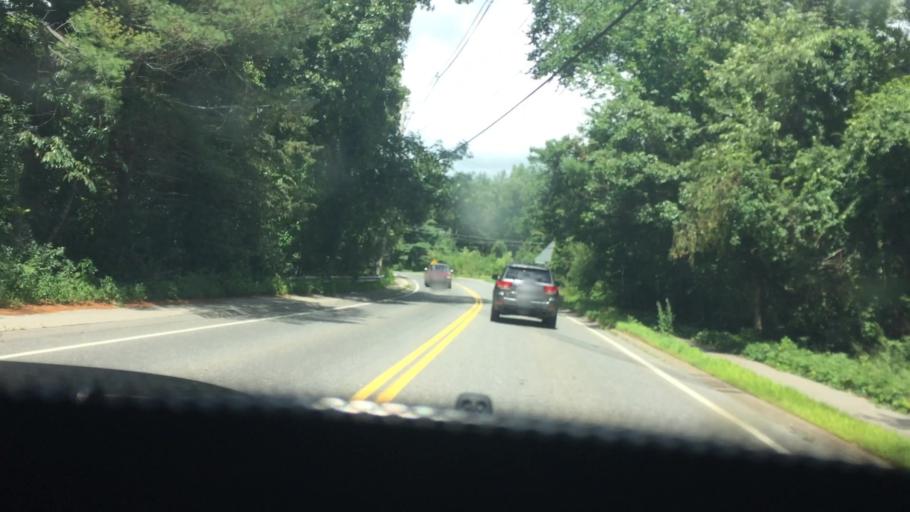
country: US
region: Massachusetts
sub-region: Middlesex County
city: Sudbury
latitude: 42.3986
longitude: -71.4317
